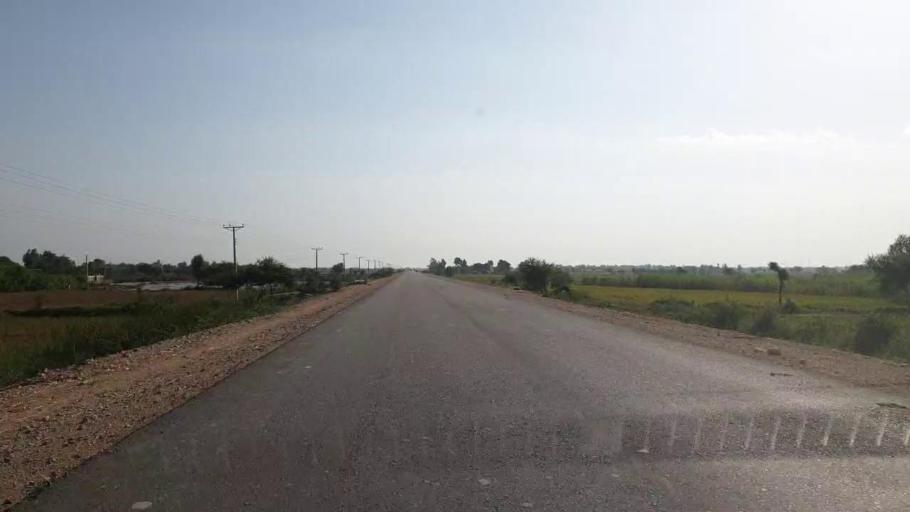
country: PK
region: Sindh
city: Tando Bago
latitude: 24.6571
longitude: 69.0069
